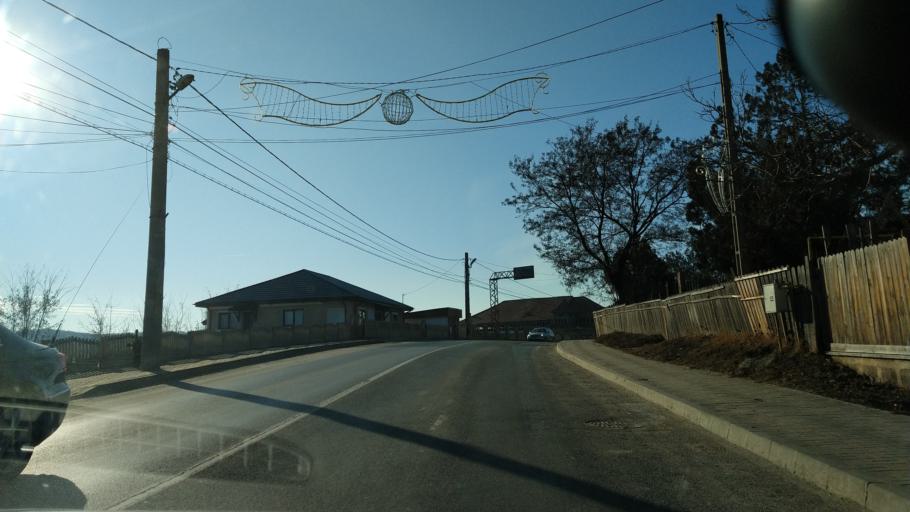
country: RO
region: Iasi
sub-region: Comuna Targu Frumos
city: Targu Frumos
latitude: 47.2034
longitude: 27.0061
